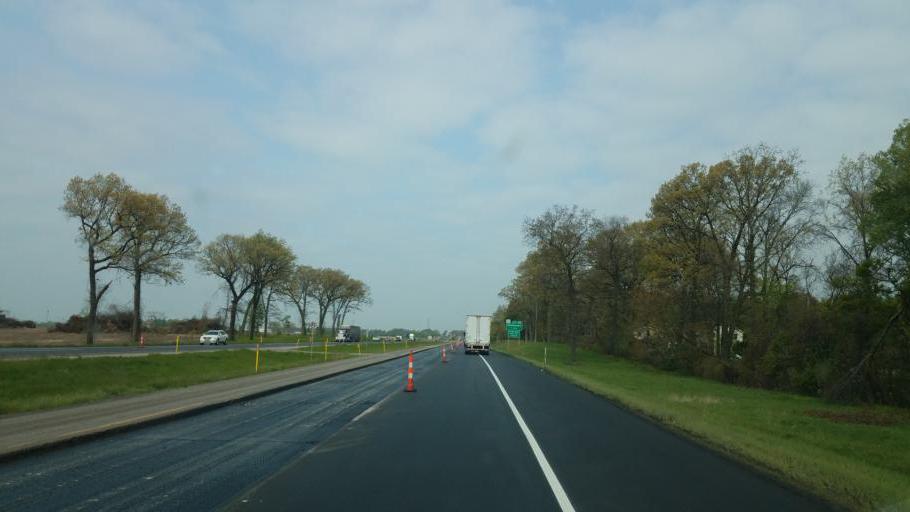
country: US
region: Indiana
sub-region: Saint Joseph County
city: Granger
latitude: 41.7340
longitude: -86.1119
